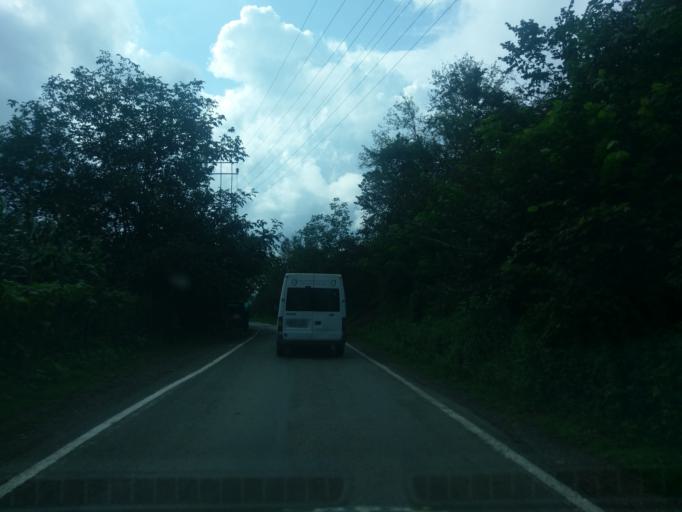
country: TR
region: Ordu
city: Camas
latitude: 40.9106
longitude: 37.6138
